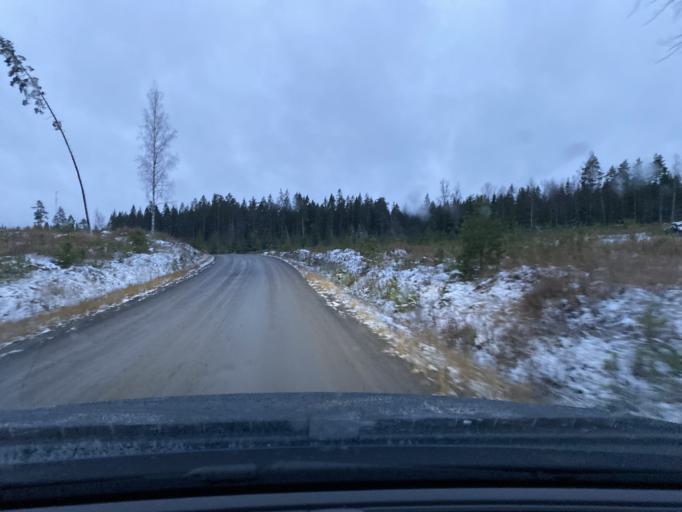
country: FI
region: Pirkanmaa
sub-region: Lounais-Pirkanmaa
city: Punkalaidun
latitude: 61.1599
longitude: 22.9455
